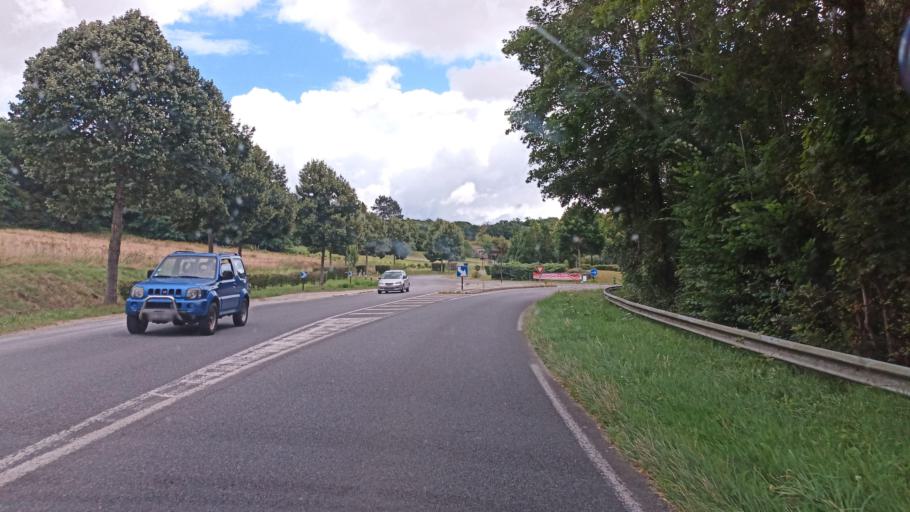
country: FR
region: Ile-de-France
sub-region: Departement de Seine-et-Marne
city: Voulx
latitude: 48.2895
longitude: 2.9552
